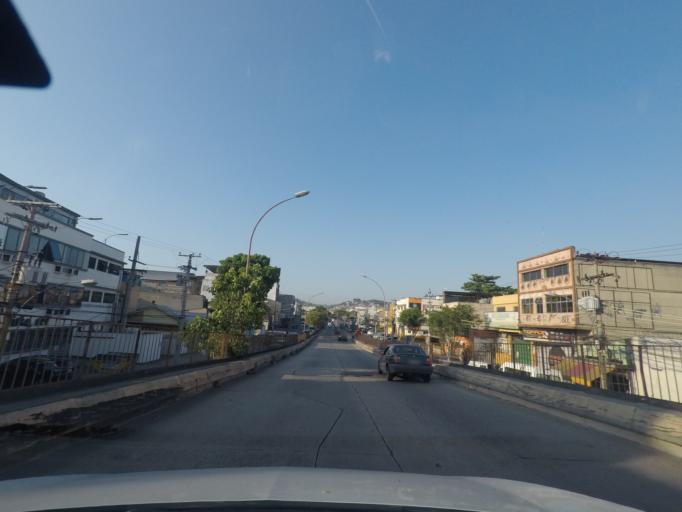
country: BR
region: Rio de Janeiro
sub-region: Duque De Caxias
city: Duque de Caxias
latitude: -22.8274
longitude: -43.2753
